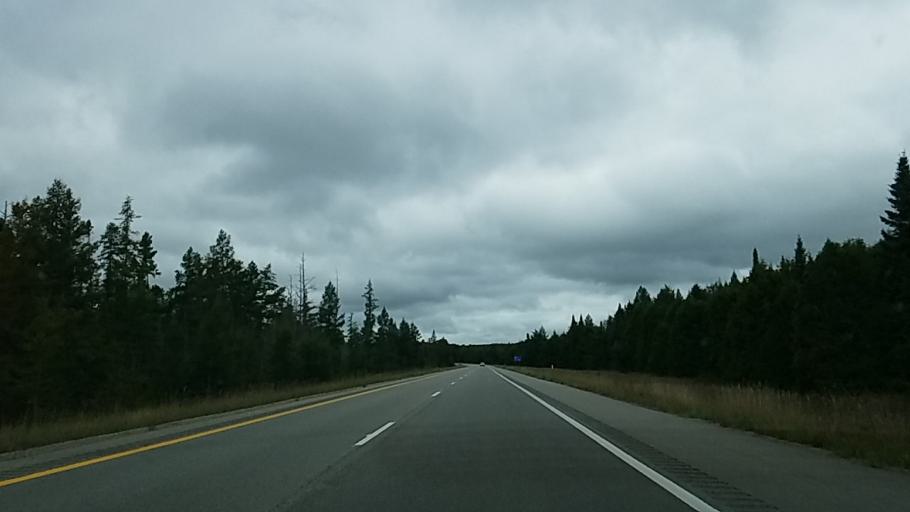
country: US
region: Michigan
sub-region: Otsego County
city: Gaylord
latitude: 45.1638
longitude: -84.6582
